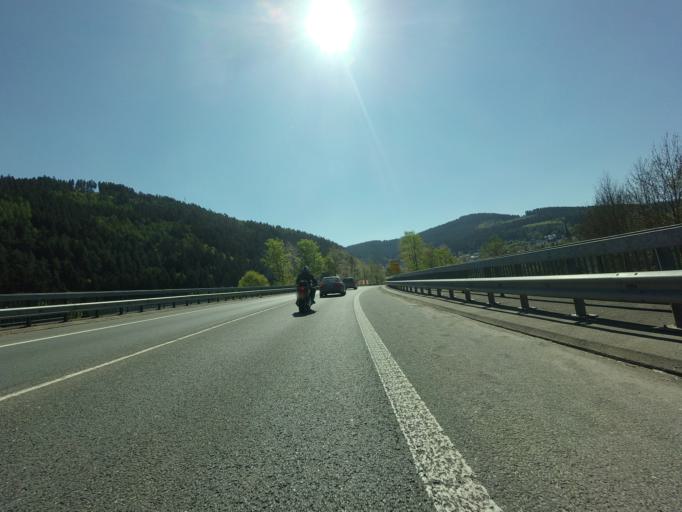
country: DE
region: North Rhine-Westphalia
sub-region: Regierungsbezirk Arnsberg
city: Lennestadt
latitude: 51.1087
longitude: 8.0717
